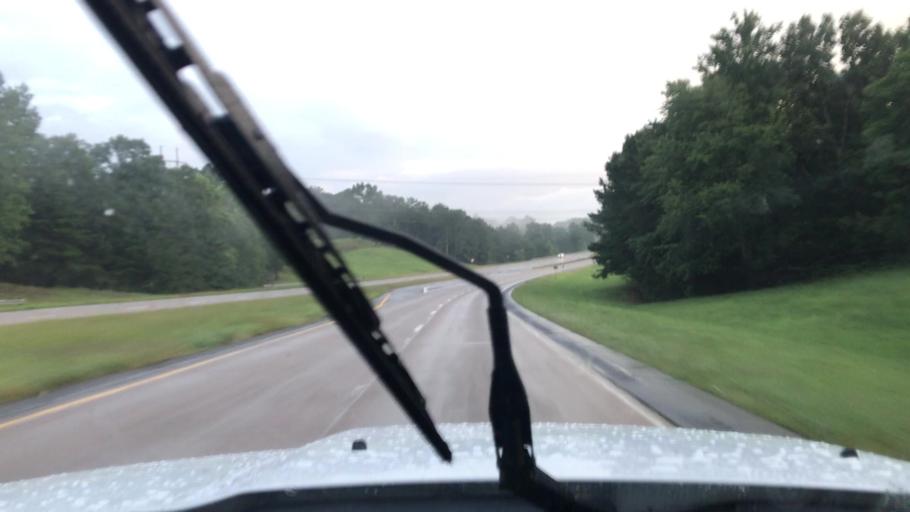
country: US
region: Georgia
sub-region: Gilmer County
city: Ellijay
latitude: 34.5959
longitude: -84.5189
